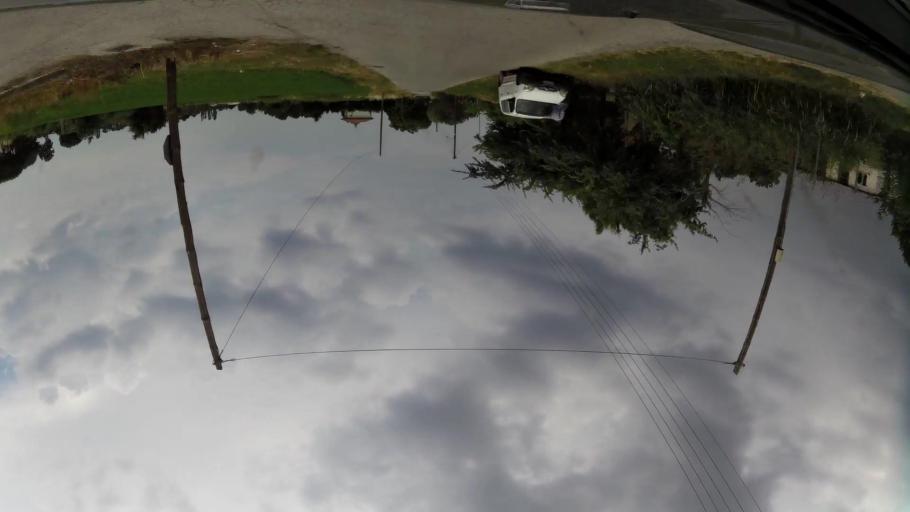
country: GR
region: Central Macedonia
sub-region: Nomos Pierias
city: Kallithea
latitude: 40.2742
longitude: 22.5836
